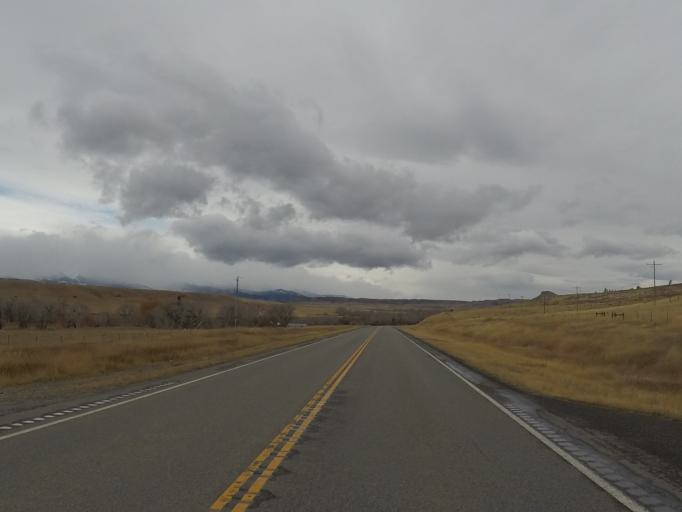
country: US
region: Montana
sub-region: Sweet Grass County
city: Big Timber
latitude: 45.9252
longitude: -109.9816
